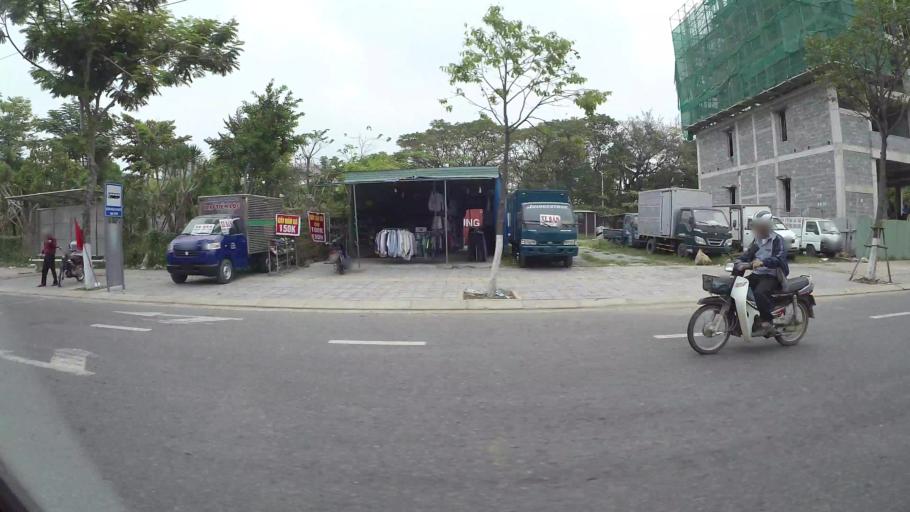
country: VN
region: Da Nang
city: Cam Le
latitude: 16.0297
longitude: 108.2088
